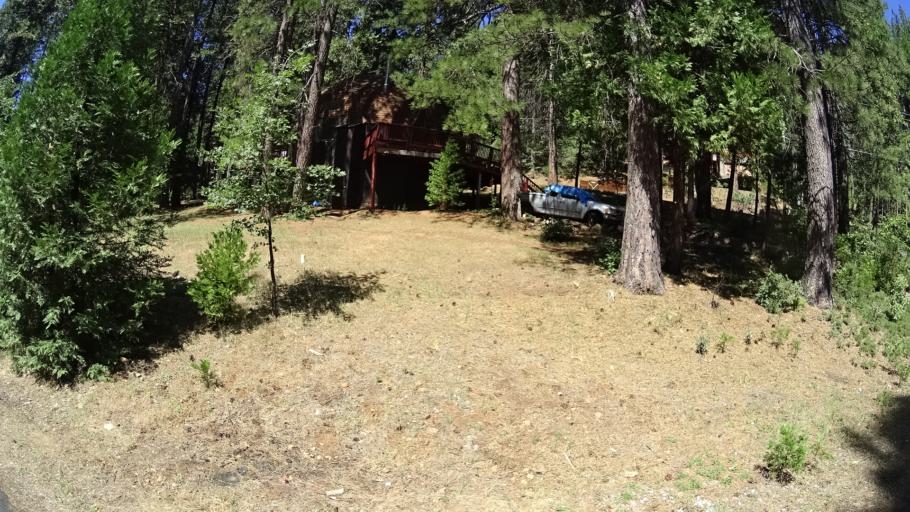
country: US
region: California
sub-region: Calaveras County
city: Arnold
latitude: 38.2411
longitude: -120.3684
